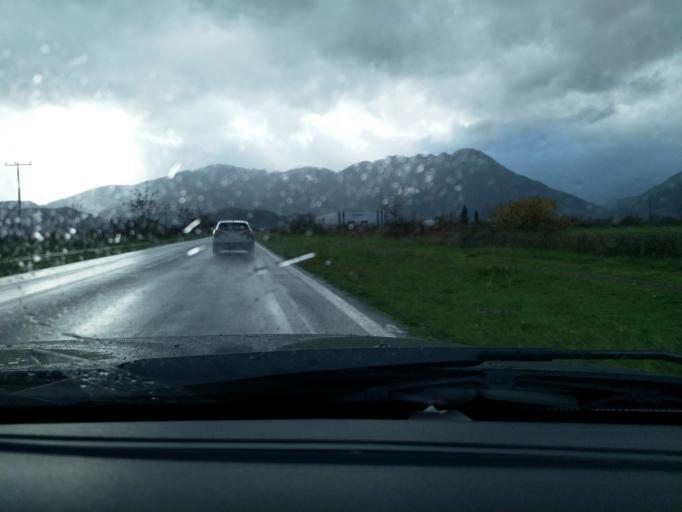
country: GR
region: Thessaly
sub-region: Trikala
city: Palaiomonastiro
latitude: 39.4801
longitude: 21.6714
